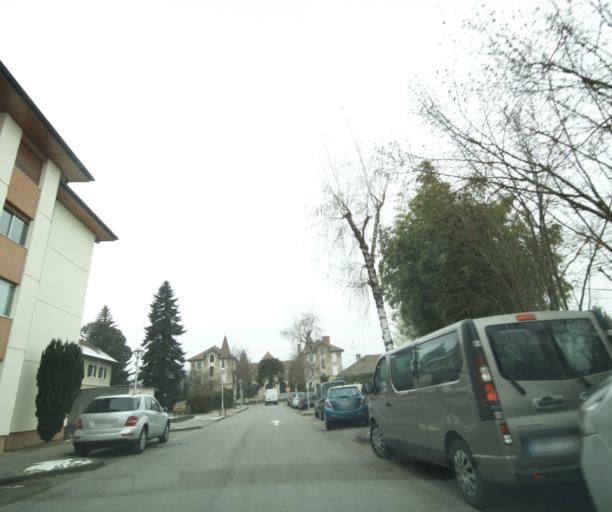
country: FR
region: Rhone-Alpes
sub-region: Departement de la Haute-Savoie
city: Reignier-Esery
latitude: 46.1352
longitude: 6.2681
